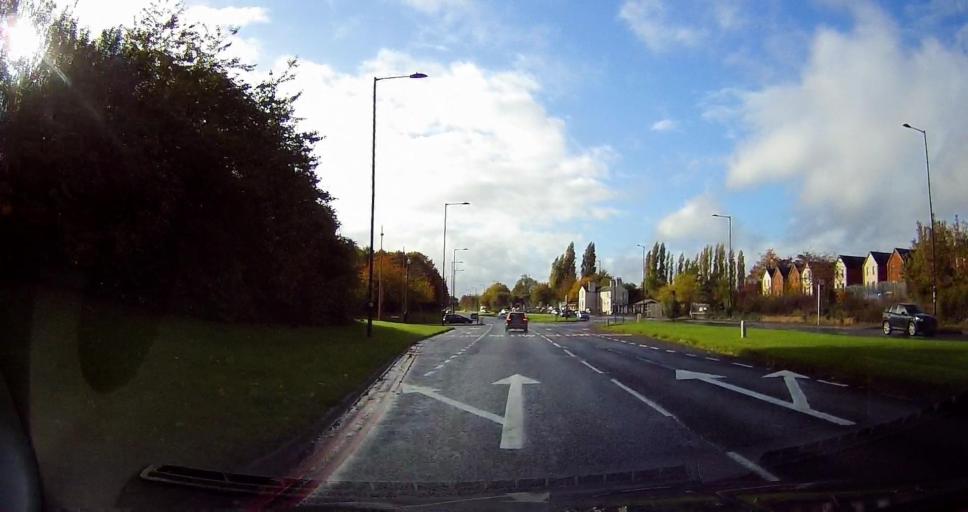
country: GB
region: England
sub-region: City and Borough of Birmingham
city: Sutton Coldfield
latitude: 52.5231
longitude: -1.7936
